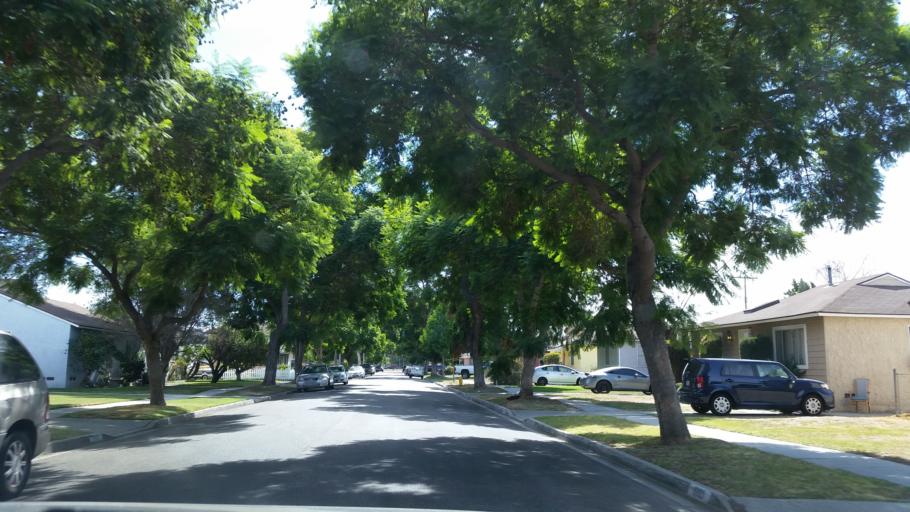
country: US
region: California
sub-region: Los Angeles County
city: Lakewood
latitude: 33.8630
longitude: -118.1375
